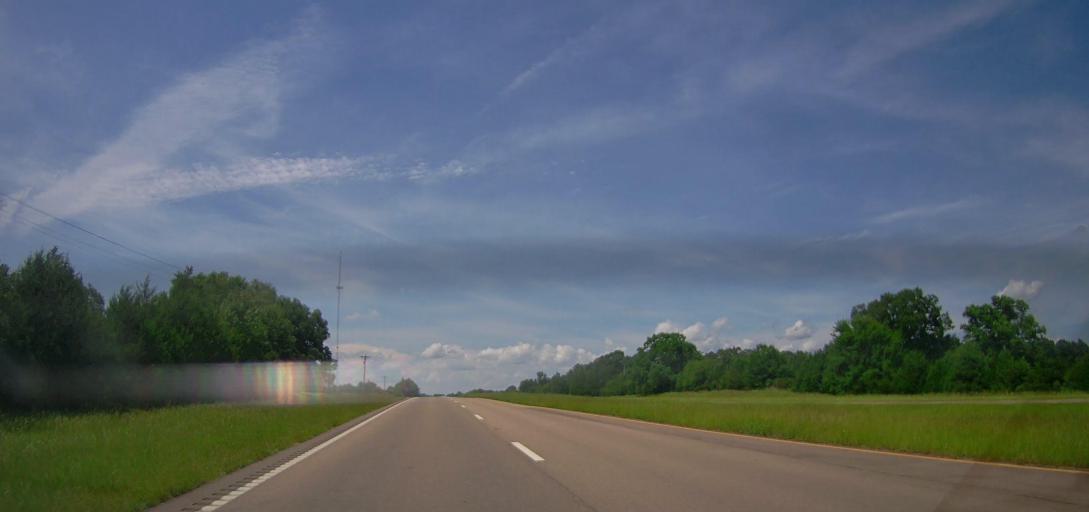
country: US
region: Mississippi
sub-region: Monroe County
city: Amory
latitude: 33.9475
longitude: -88.6019
